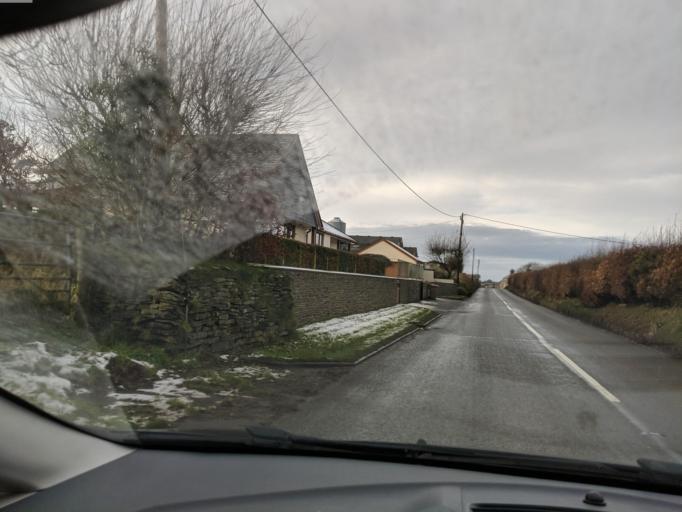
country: GB
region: England
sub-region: Cornwall
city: Jacobstow
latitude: 50.6629
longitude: -4.5813
